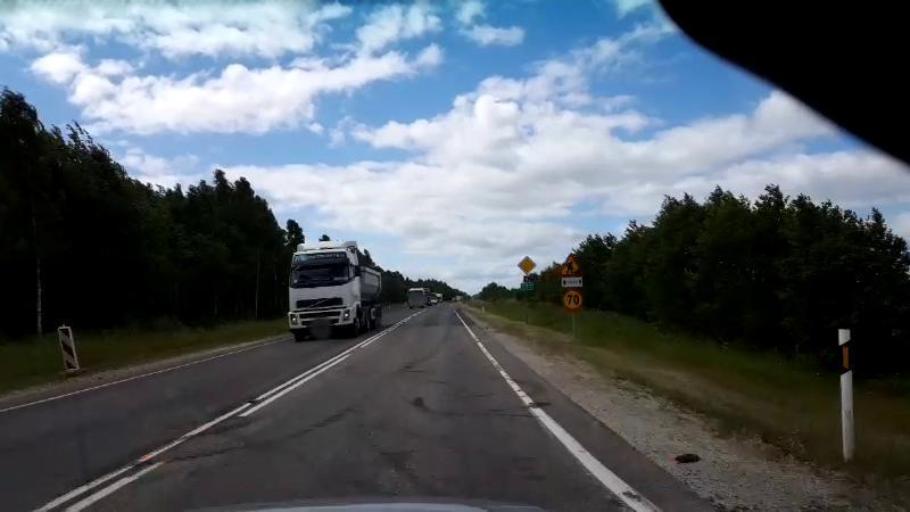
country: LV
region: Salacgrivas
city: Ainazi
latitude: 58.0078
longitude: 24.4879
